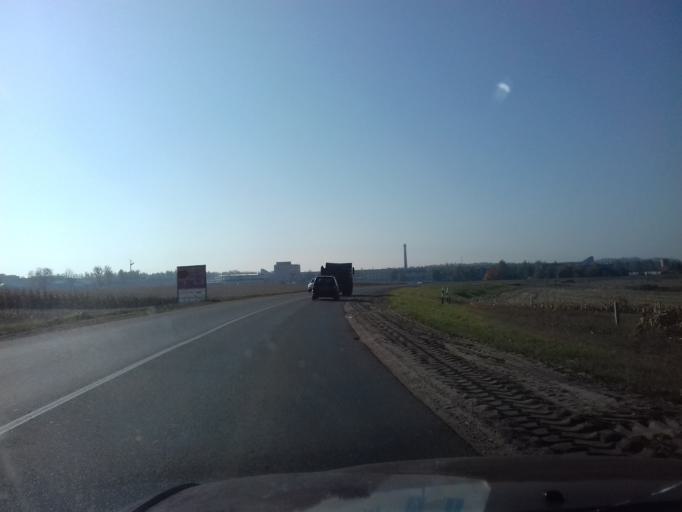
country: BY
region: Minsk
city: Hatava
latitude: 53.7823
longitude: 27.6543
